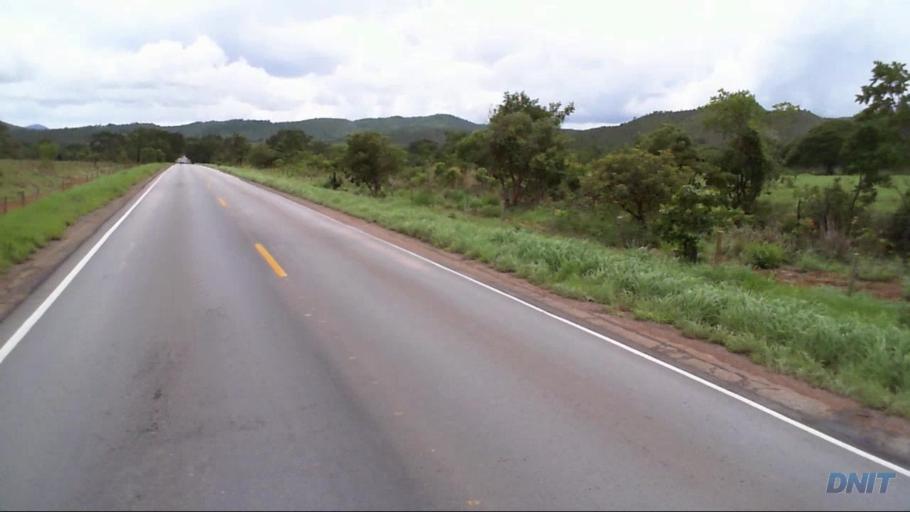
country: BR
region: Goias
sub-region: Padre Bernardo
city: Padre Bernardo
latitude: -15.4513
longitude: -48.2089
